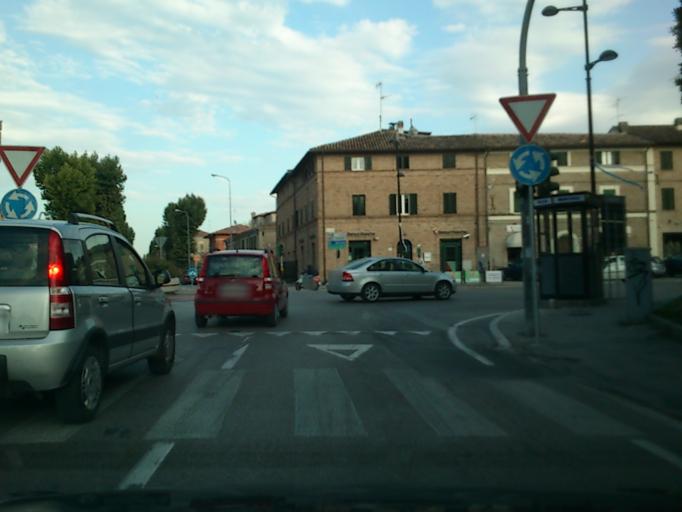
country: IT
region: The Marches
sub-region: Provincia di Pesaro e Urbino
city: Fano
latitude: 43.8425
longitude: 13.0133
